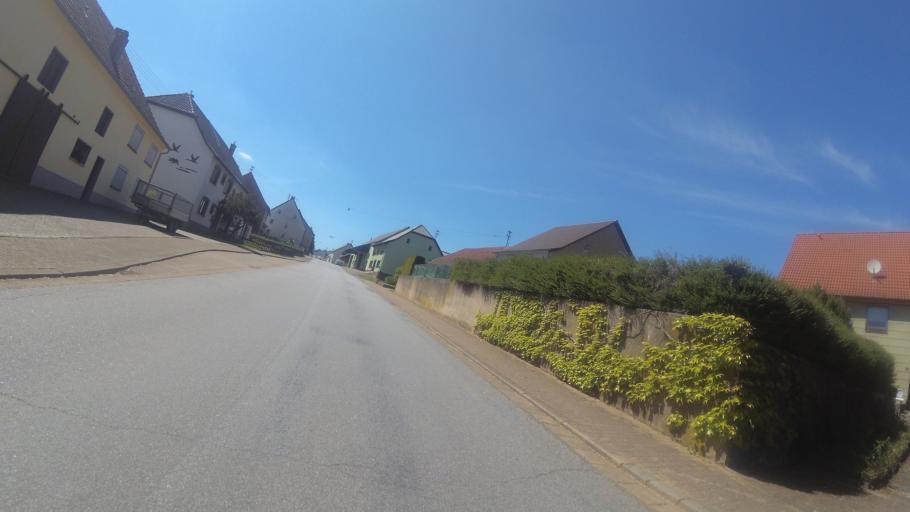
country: DE
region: Saarland
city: Heusweiler
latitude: 49.3508
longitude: 6.9251
